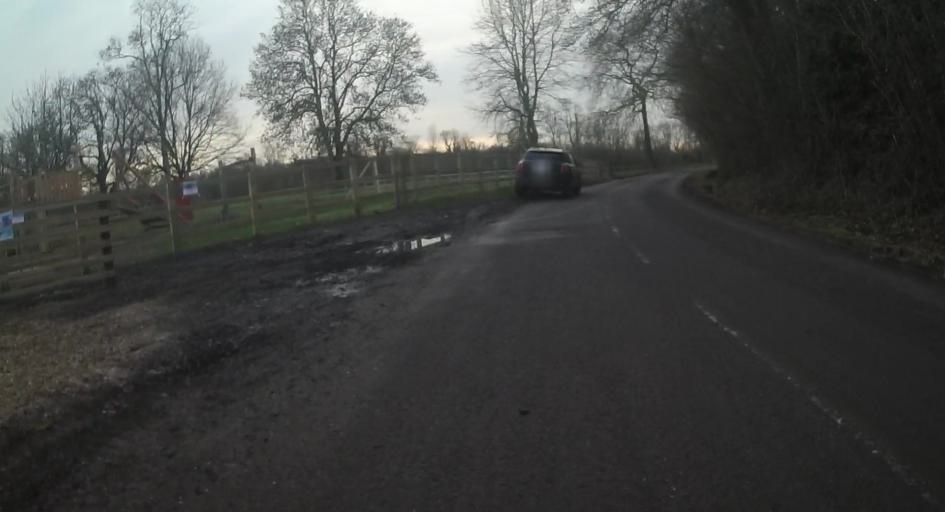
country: GB
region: England
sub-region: Hampshire
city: Andover
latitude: 51.1964
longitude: -1.3847
